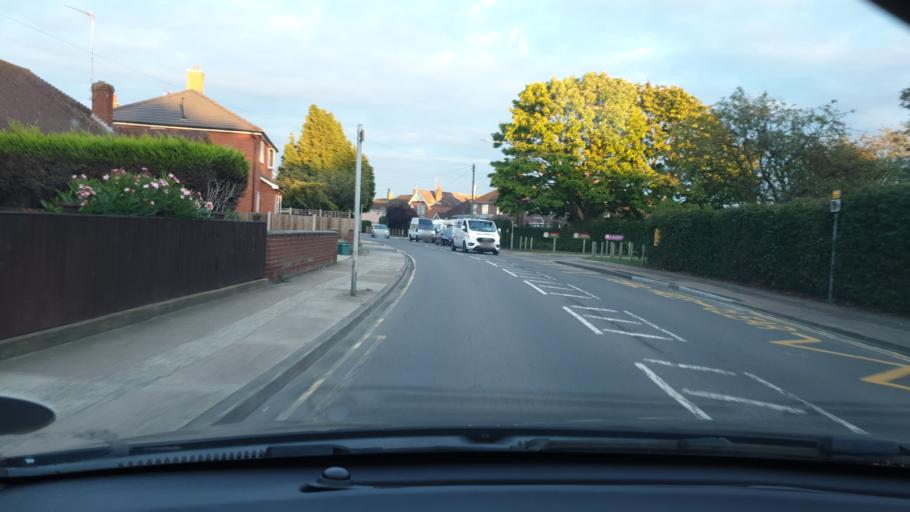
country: GB
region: England
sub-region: Essex
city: Colchester
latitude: 51.8961
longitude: 0.9394
